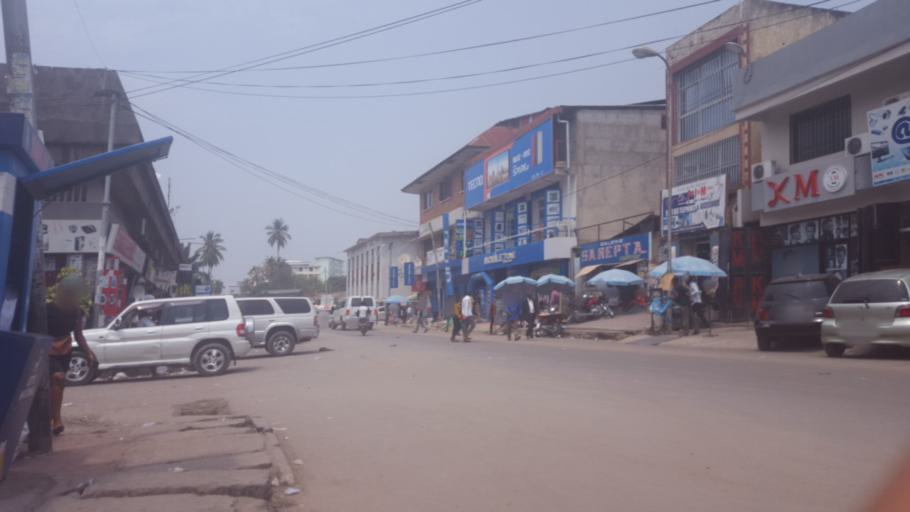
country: CD
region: Kinshasa
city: Kinshasa
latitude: -4.3046
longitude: 15.3131
